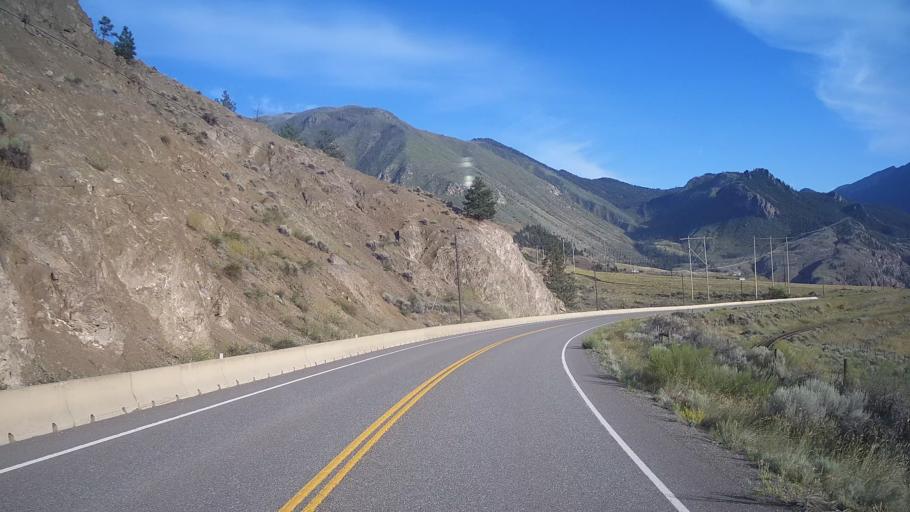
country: CA
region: British Columbia
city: Lillooet
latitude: 50.7776
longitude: -121.8386
